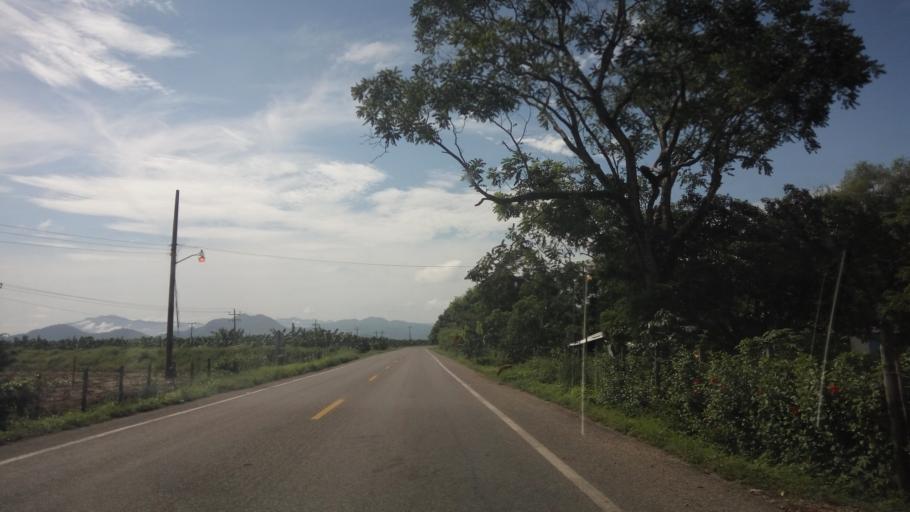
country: MX
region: Tabasco
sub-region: Teapa
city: Eureka y Belen
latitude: 17.6271
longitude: -92.9633
